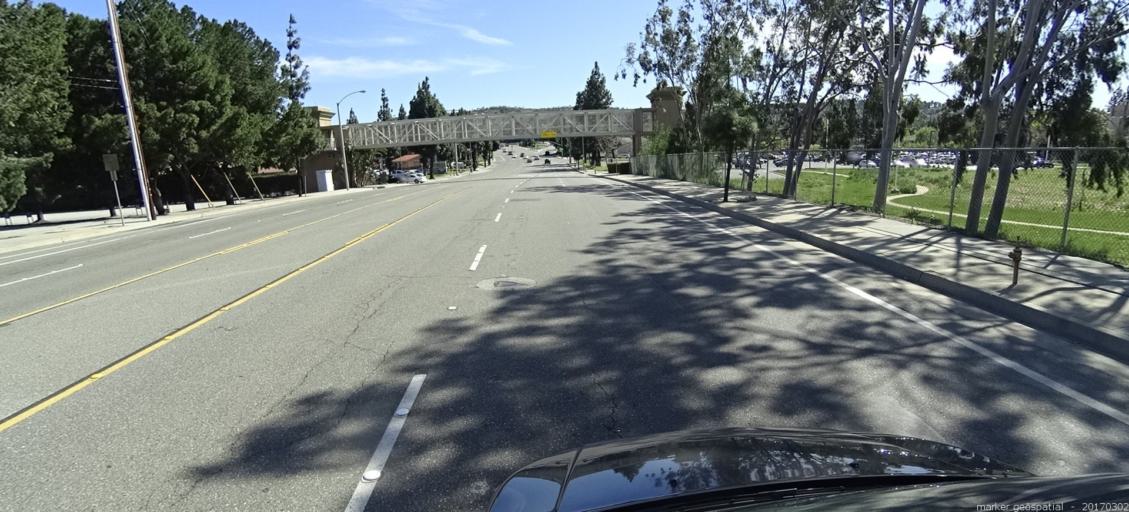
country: US
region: California
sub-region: Orange County
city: Yorba Linda
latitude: 33.8546
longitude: -117.8168
